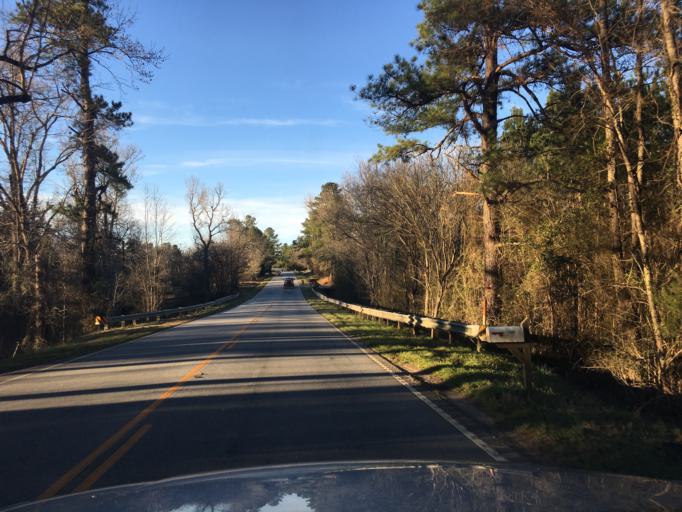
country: US
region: South Carolina
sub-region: Saluda County
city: Saluda
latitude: 34.0658
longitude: -81.8175
